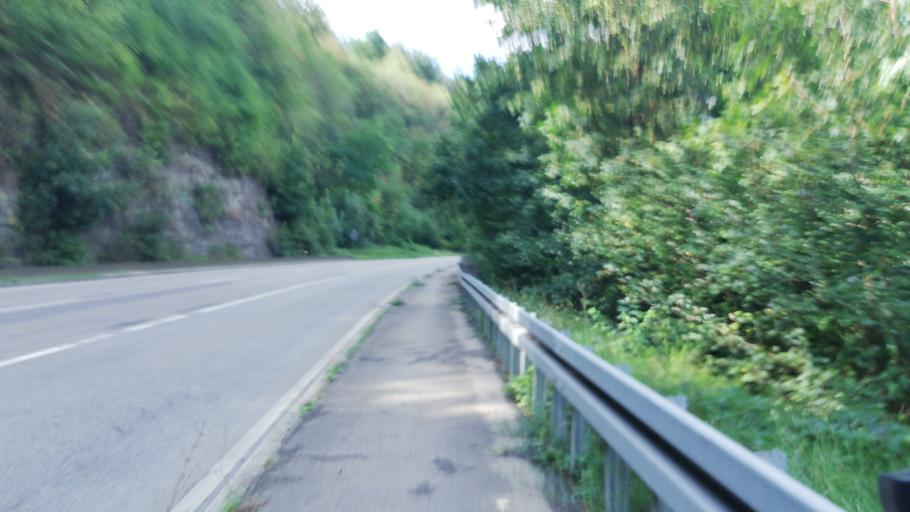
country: DE
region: Baden-Wuerttemberg
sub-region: Regierungsbezirk Stuttgart
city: Stuttgart Muehlhausen
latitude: 48.8665
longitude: 9.2759
